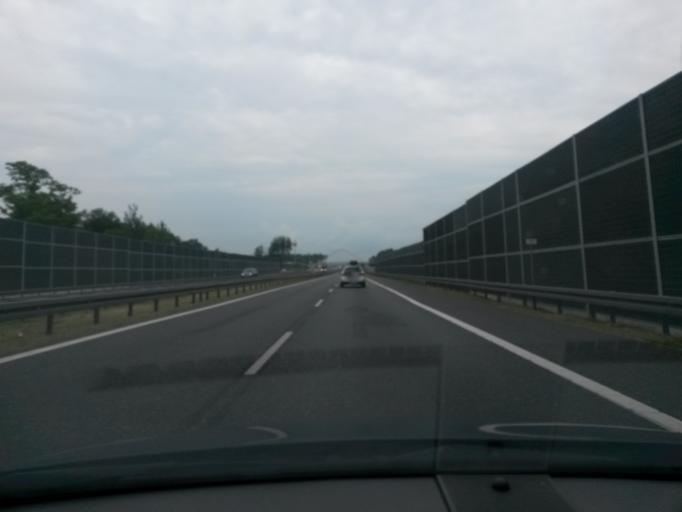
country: PL
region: Masovian Voivodeship
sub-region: Powiat zyrardowski
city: Mszczonow
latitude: 51.9567
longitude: 20.4957
